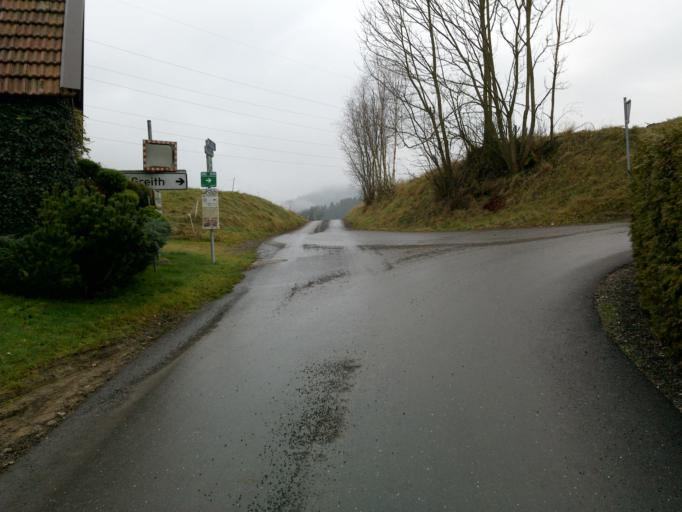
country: AT
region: Styria
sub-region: Politischer Bezirk Murtal
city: Feistritz bei Knittelfeld
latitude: 47.2909
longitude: 14.9018
